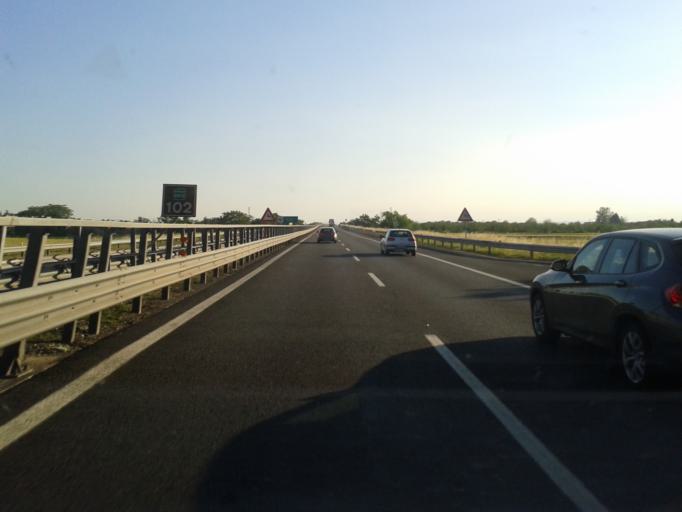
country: IT
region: Piedmont
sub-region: Provincia di Alessandria
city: Pozzolo Formigaro
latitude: 44.8140
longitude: 8.7729
